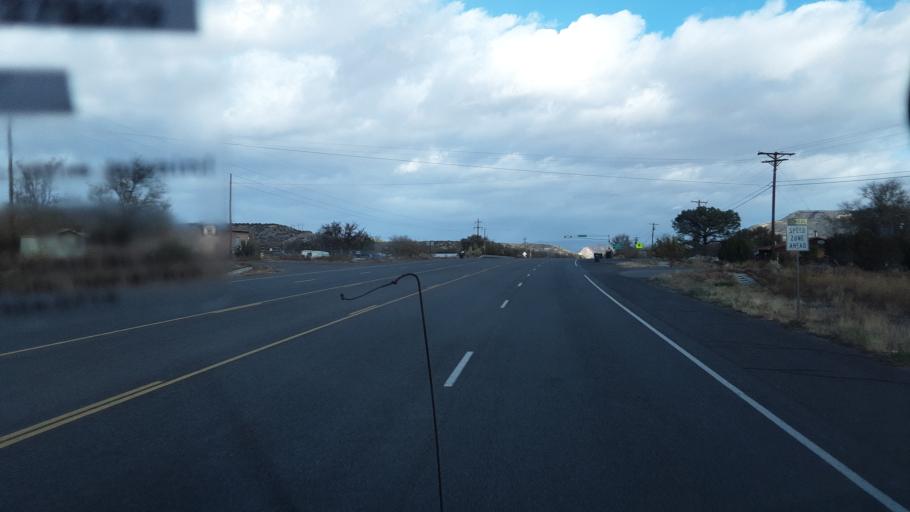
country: US
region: New Mexico
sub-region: Rio Arriba County
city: Ohkay Owingeh
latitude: 36.0520
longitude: -106.1142
